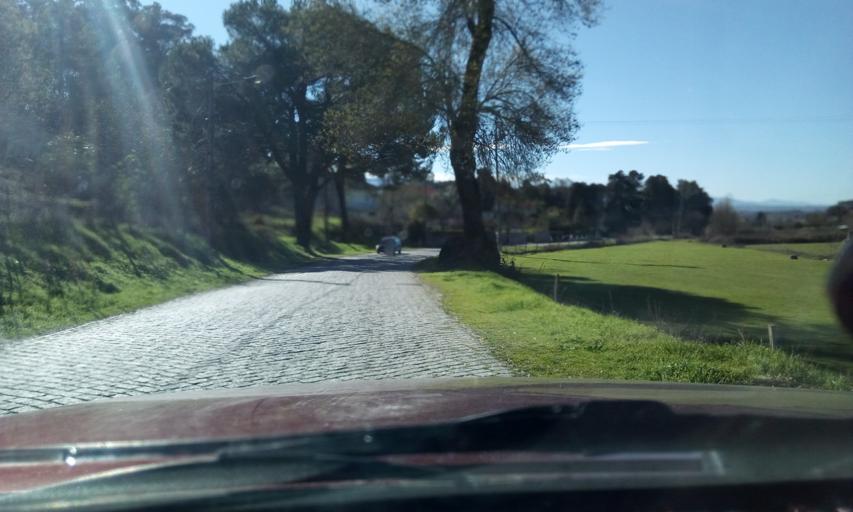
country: PT
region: Guarda
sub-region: Fornos de Algodres
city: Fornos de Algodres
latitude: 40.6207
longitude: -7.5302
